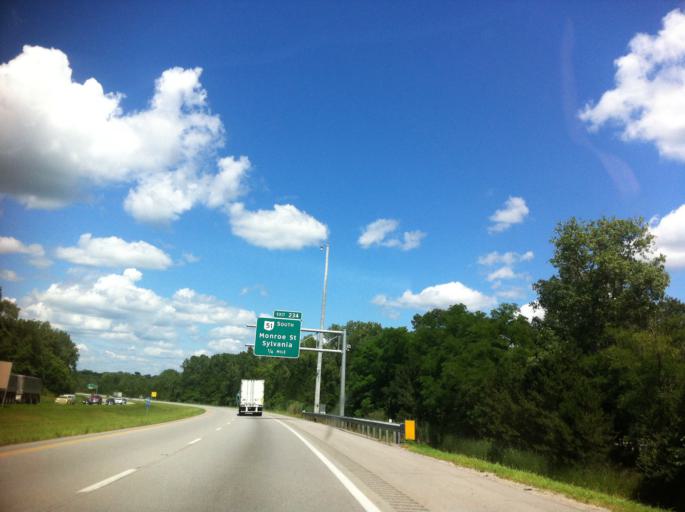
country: US
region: Ohio
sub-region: Lucas County
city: Sylvania
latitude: 41.7039
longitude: -83.6911
